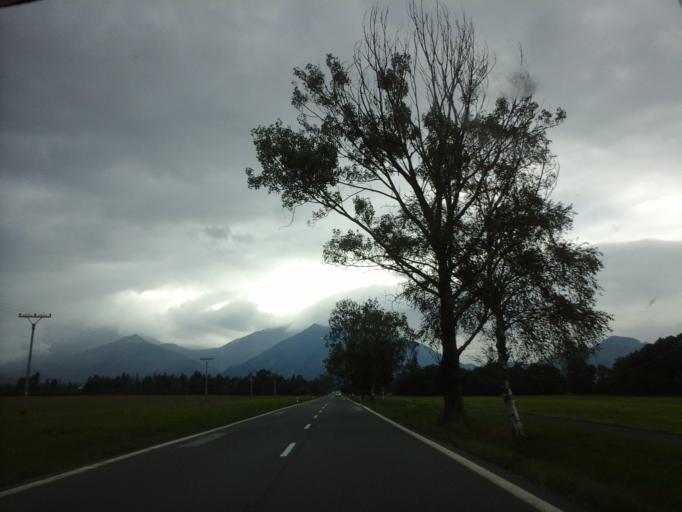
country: SK
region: Presovsky
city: Spisska Bela
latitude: 49.2074
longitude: 20.3864
